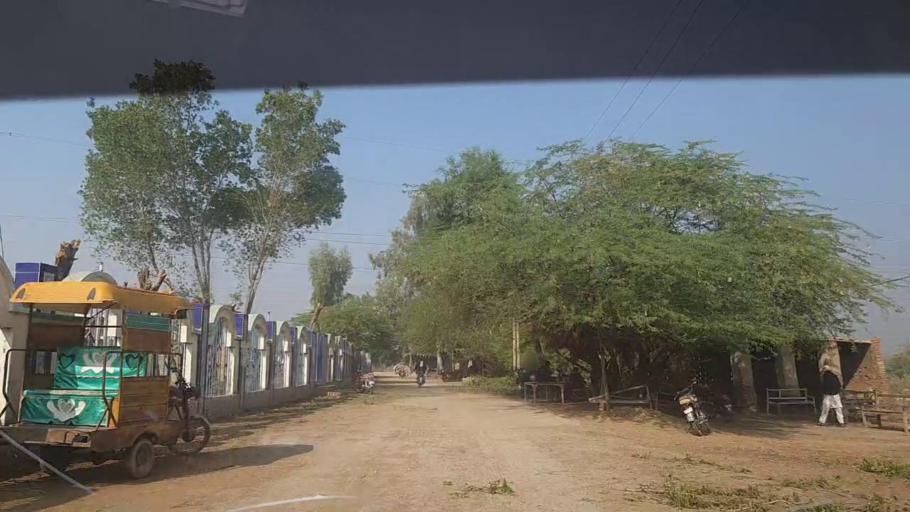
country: PK
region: Sindh
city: Khairpur
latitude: 27.4712
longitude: 68.7090
